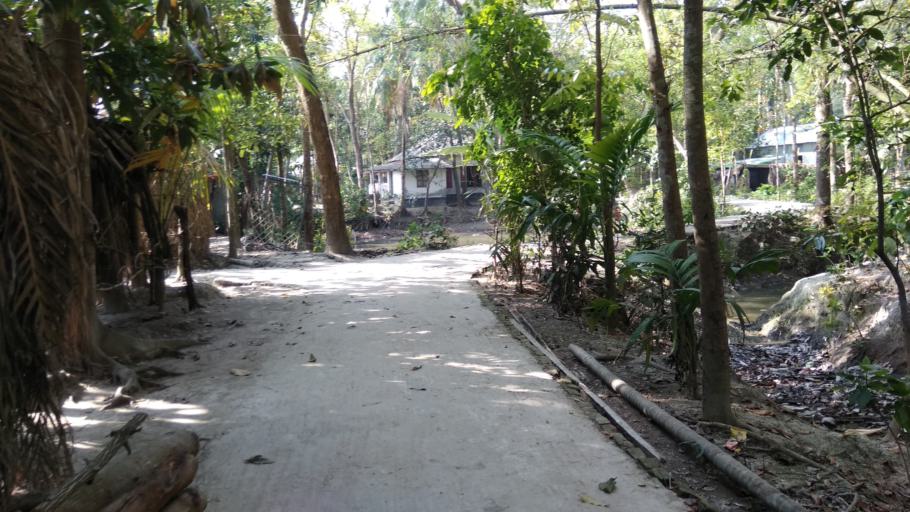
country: BD
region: Barisal
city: Mehendiganj
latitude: 22.9383
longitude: 90.4138
